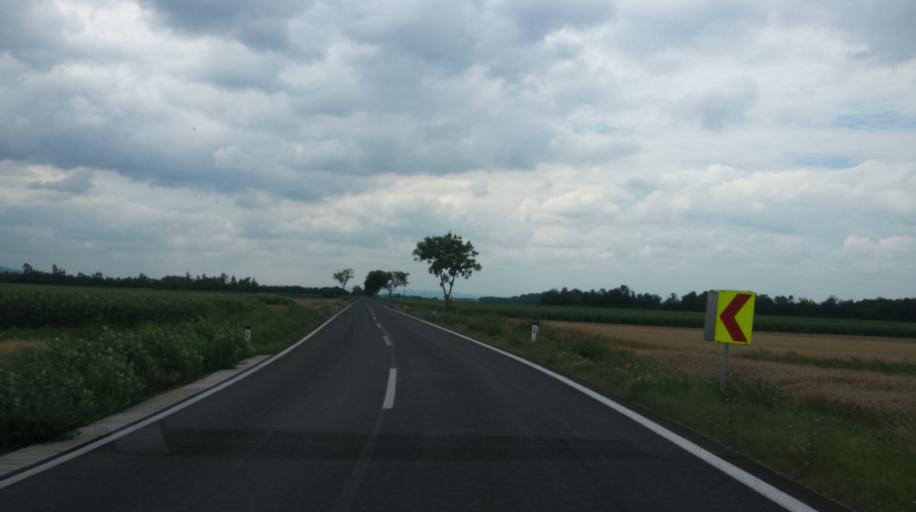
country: AT
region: Lower Austria
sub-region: Politischer Bezirk Wien-Umgebung
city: Moosbrunn
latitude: 48.0035
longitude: 16.4459
